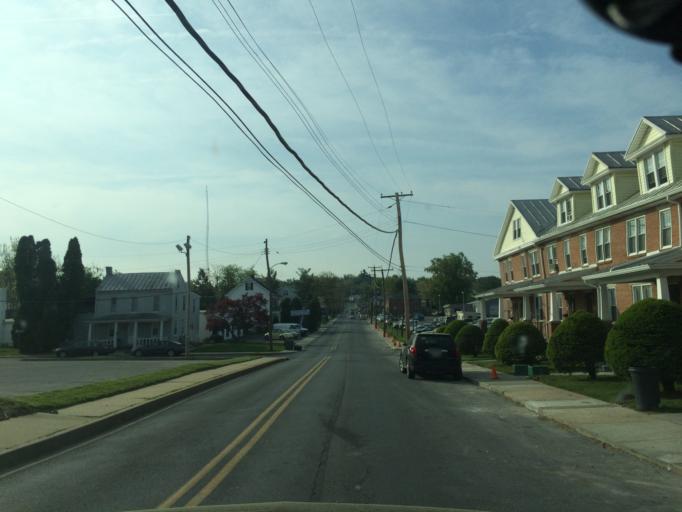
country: US
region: Maryland
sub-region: Carroll County
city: Westminster
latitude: 39.5693
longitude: -76.9921
